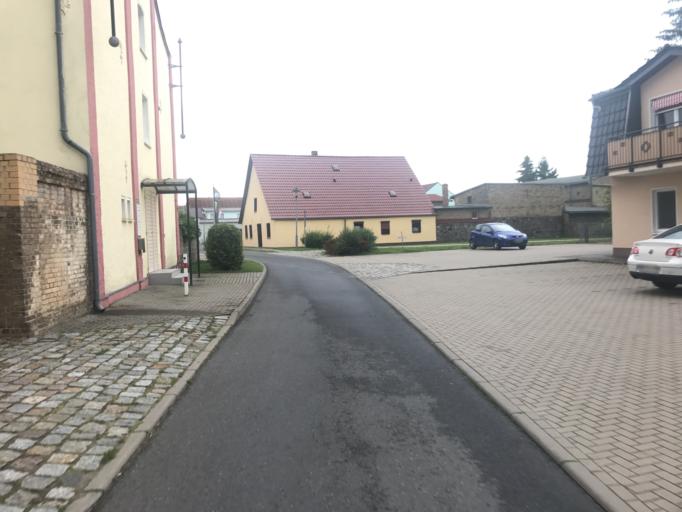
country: DE
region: Brandenburg
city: Melchow
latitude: 52.8472
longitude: 13.6839
